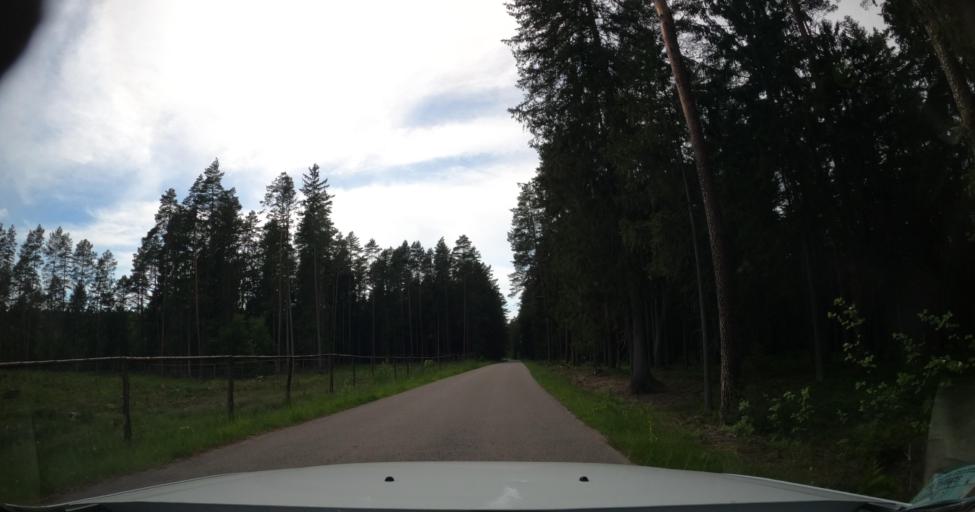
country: PL
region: Warmian-Masurian Voivodeship
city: Dobre Miasto
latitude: 54.1043
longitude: 20.3614
